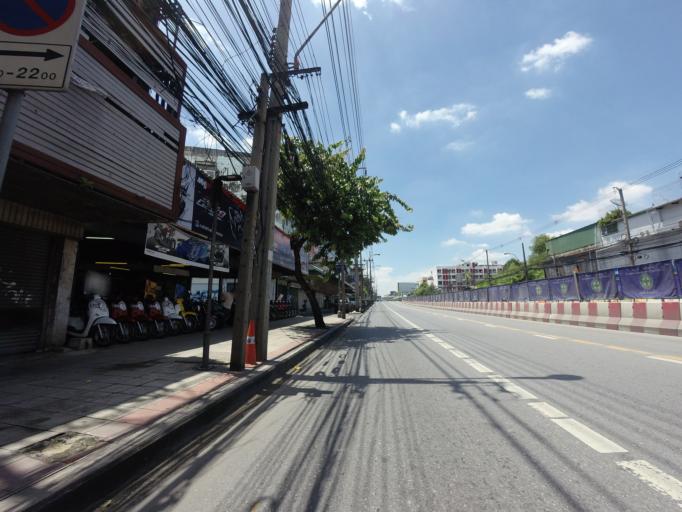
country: TH
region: Bangkok
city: Lat Phrao
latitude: 13.7995
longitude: 100.5855
